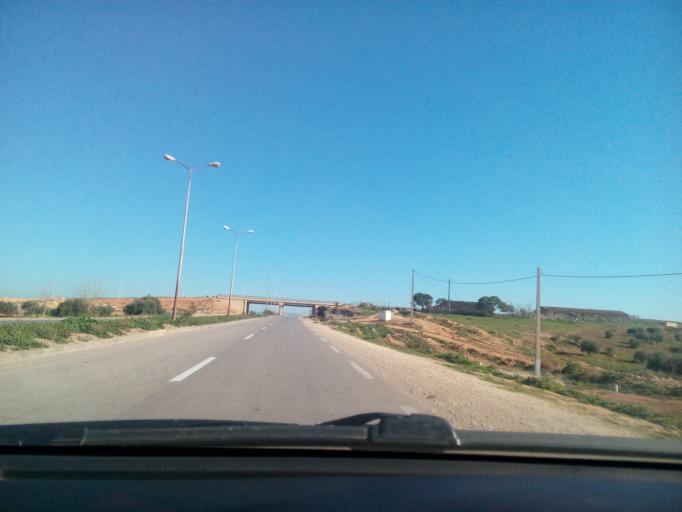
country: DZ
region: Relizane
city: Relizane
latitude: 35.7118
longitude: 0.5259
